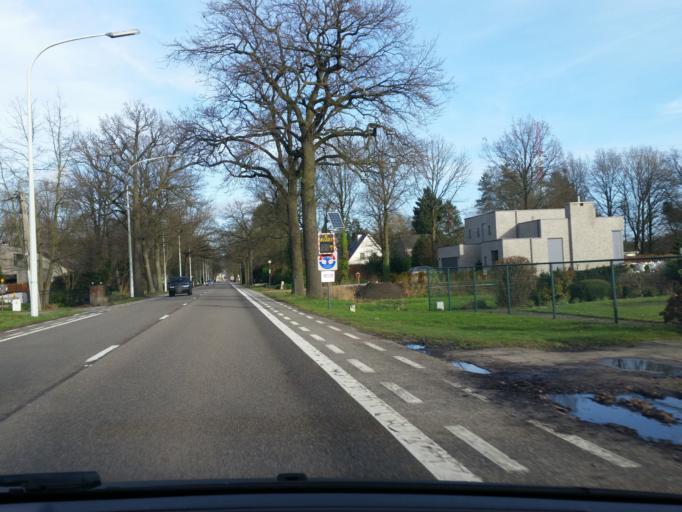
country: BE
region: Flanders
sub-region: Provincie Antwerpen
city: Brasschaat
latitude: 51.3455
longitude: 4.5371
